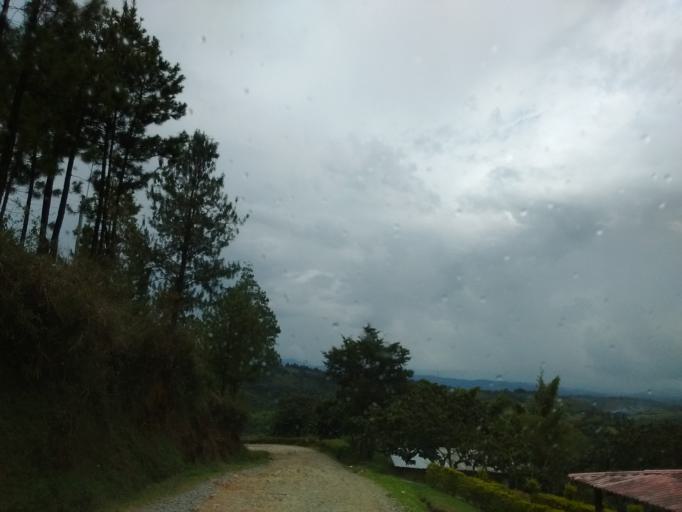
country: CO
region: Cauca
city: Cajibio
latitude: 2.5607
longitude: -76.6354
